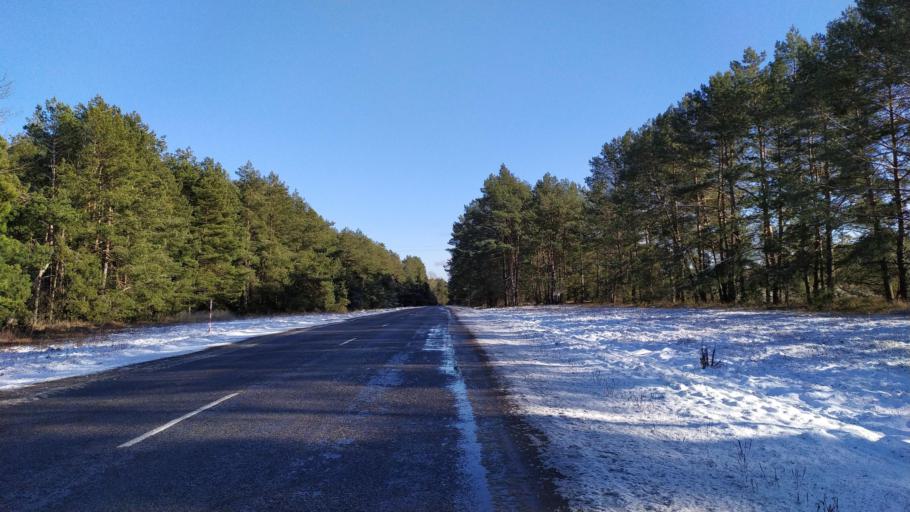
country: BY
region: Brest
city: Kamyanyets
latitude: 52.3860
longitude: 23.8505
